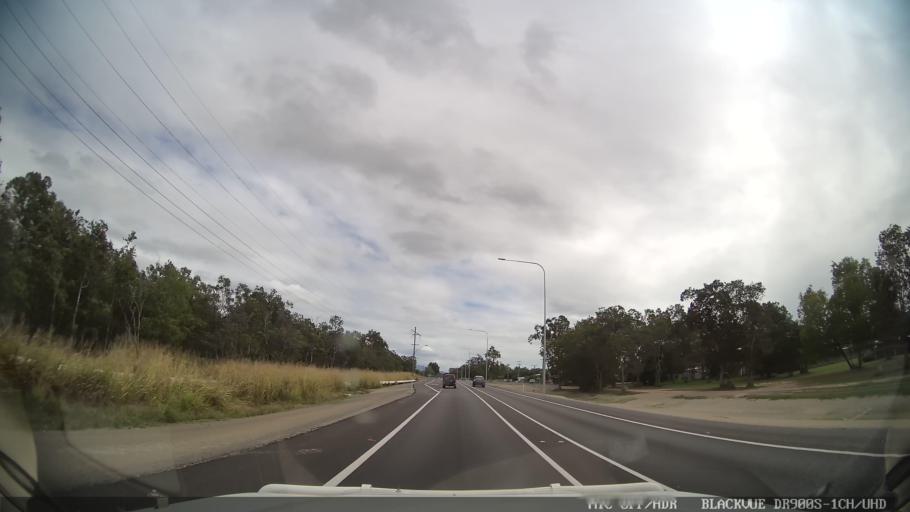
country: AU
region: Queensland
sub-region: Townsville
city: Bohle Plains
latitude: -19.1787
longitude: 146.5561
